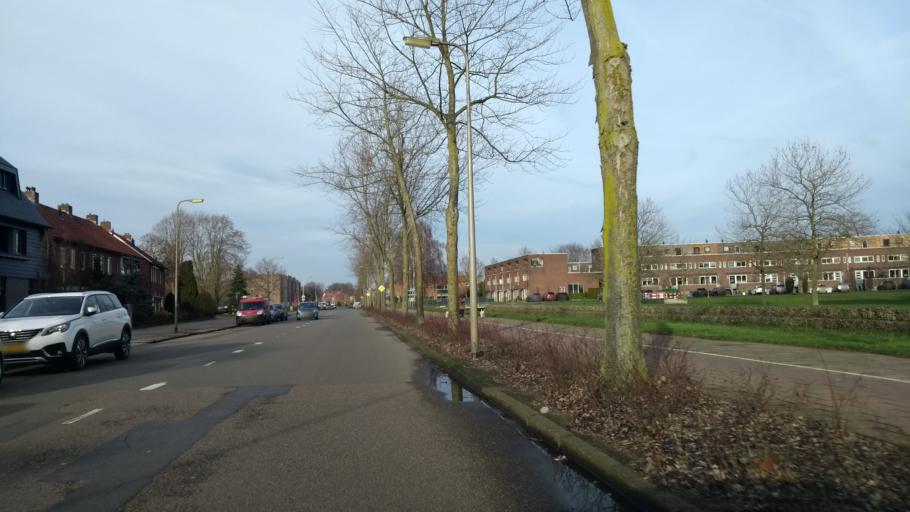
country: NL
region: Overijssel
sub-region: Gemeente Hengelo
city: Hengelo
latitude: 52.2686
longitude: 6.7857
